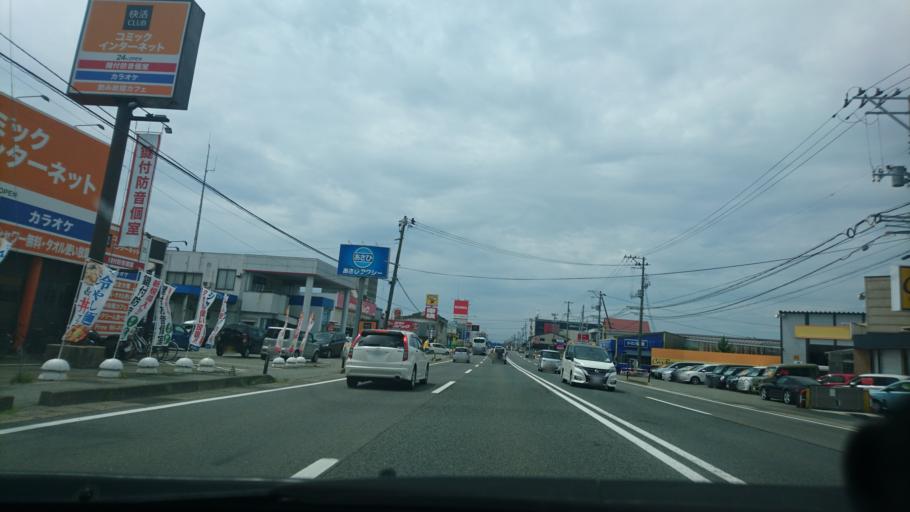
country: JP
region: Akita
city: Akita
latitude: 39.6986
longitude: 140.1153
